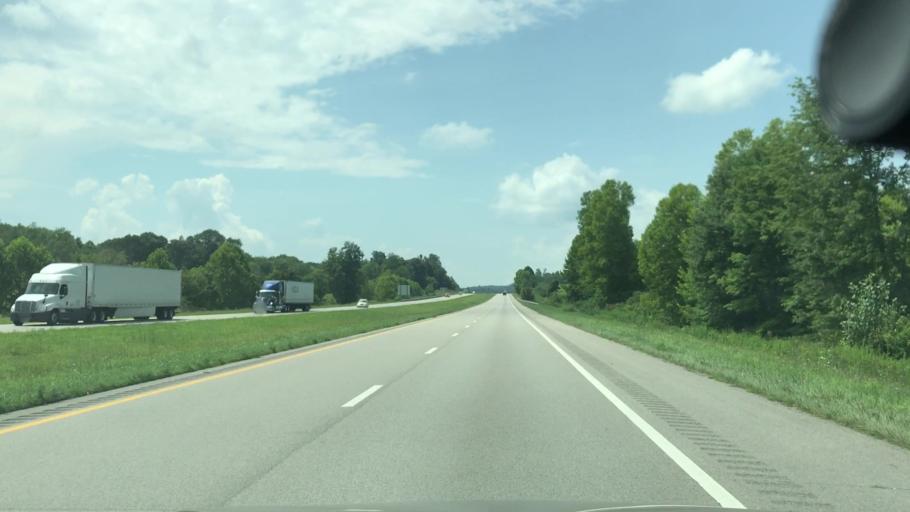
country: US
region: Ohio
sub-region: Jackson County
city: Oak Hill
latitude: 38.8872
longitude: -82.3975
